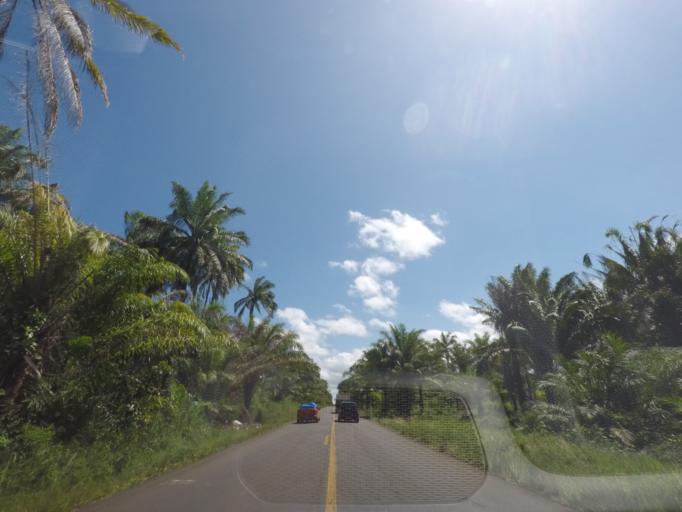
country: BR
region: Bahia
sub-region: Taperoa
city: Taperoa
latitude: -13.4719
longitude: -39.0887
